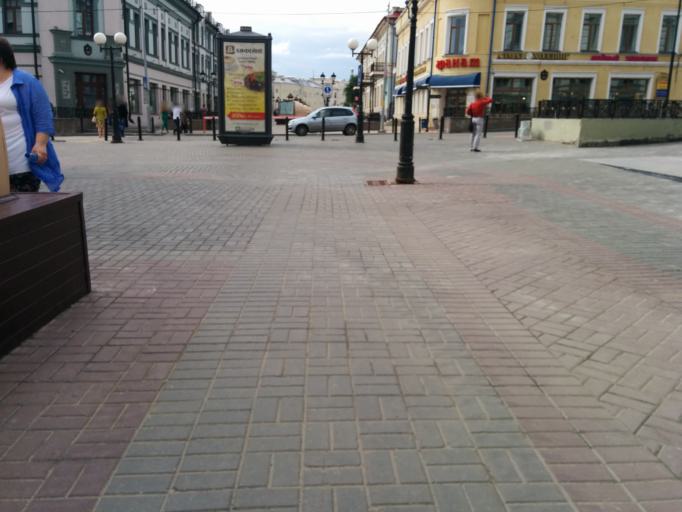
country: RU
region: Tatarstan
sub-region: Gorod Kazan'
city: Kazan
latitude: 55.7928
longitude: 49.1109
